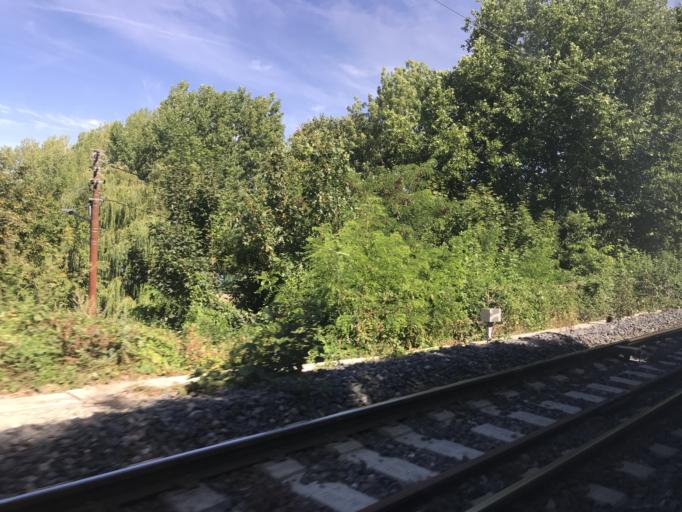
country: FR
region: Champagne-Ardenne
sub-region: Departement de la Marne
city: Reims
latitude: 49.2537
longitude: 4.0171
